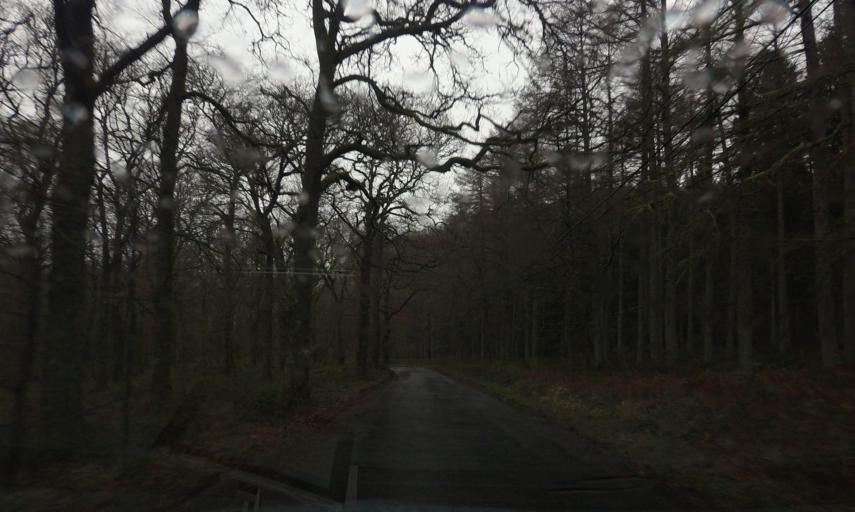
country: GB
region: Scotland
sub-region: West Dunbartonshire
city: Balloch
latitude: 56.1283
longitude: -4.6074
